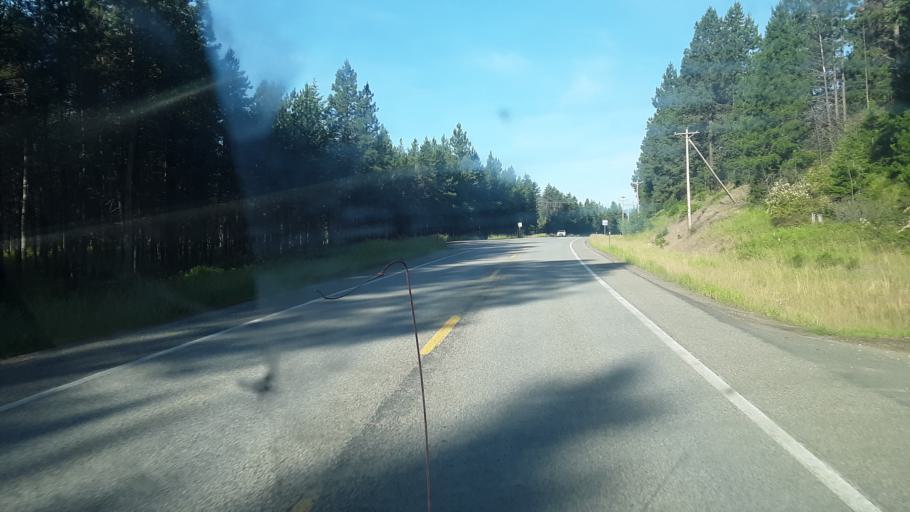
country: US
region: Idaho
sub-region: Boundary County
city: Bonners Ferry
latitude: 48.7290
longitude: -116.1967
